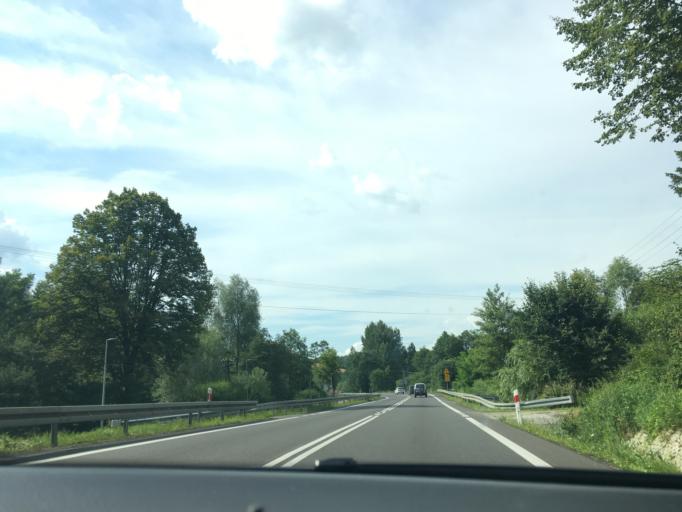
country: PL
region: Subcarpathian Voivodeship
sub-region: Powiat strzyzowski
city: Babica
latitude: 49.9241
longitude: 21.8775
